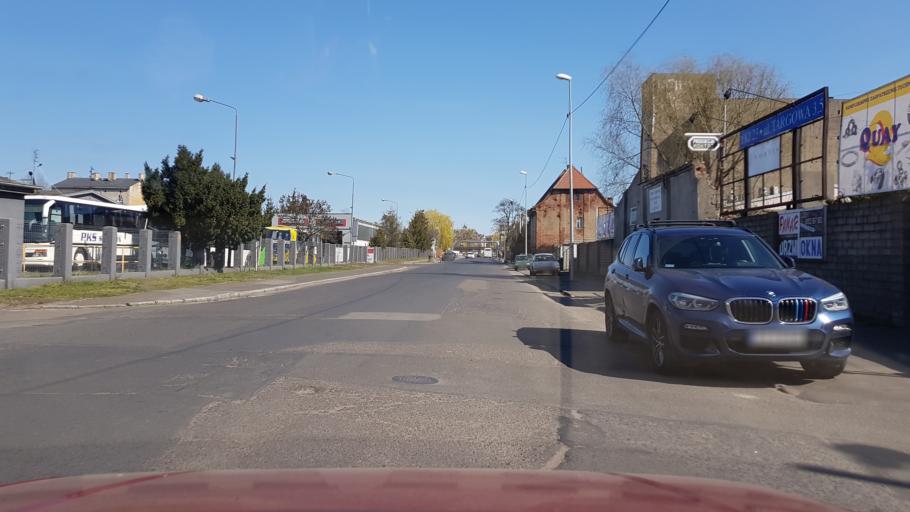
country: PL
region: West Pomeranian Voivodeship
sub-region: Szczecin
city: Szczecin
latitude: 53.4161
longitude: 14.5558
